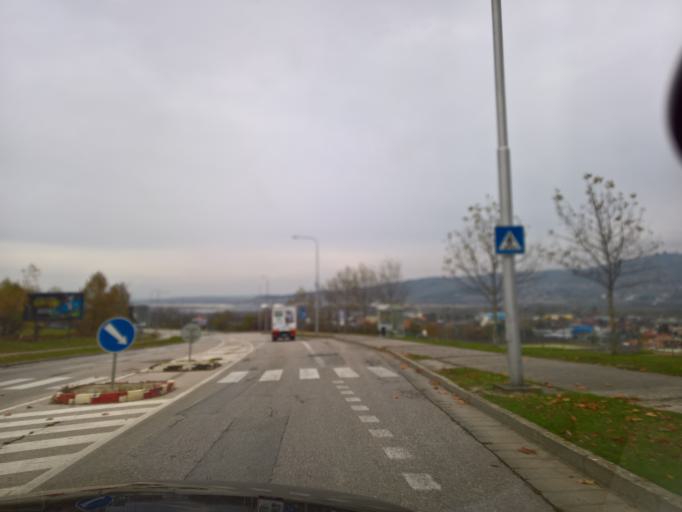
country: SK
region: Nitriansky
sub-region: Okres Nitra
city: Nitra
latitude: 48.3062
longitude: 18.0514
